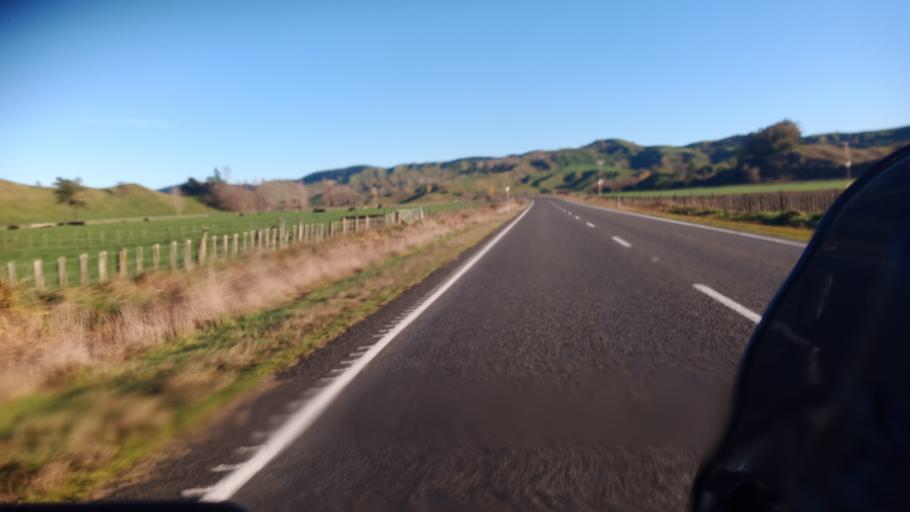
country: NZ
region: Hawke's Bay
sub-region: Wairoa District
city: Wairoa
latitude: -39.0187
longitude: 177.3719
